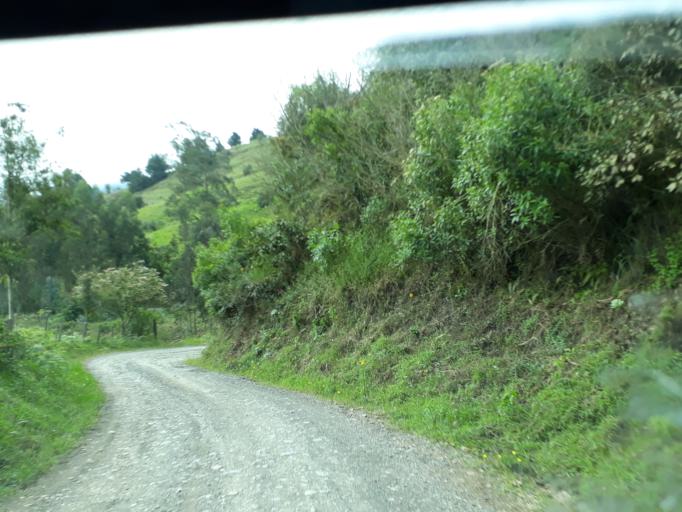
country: CO
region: Cundinamarca
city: Carmen de Carupa
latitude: 5.3765
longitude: -73.9817
